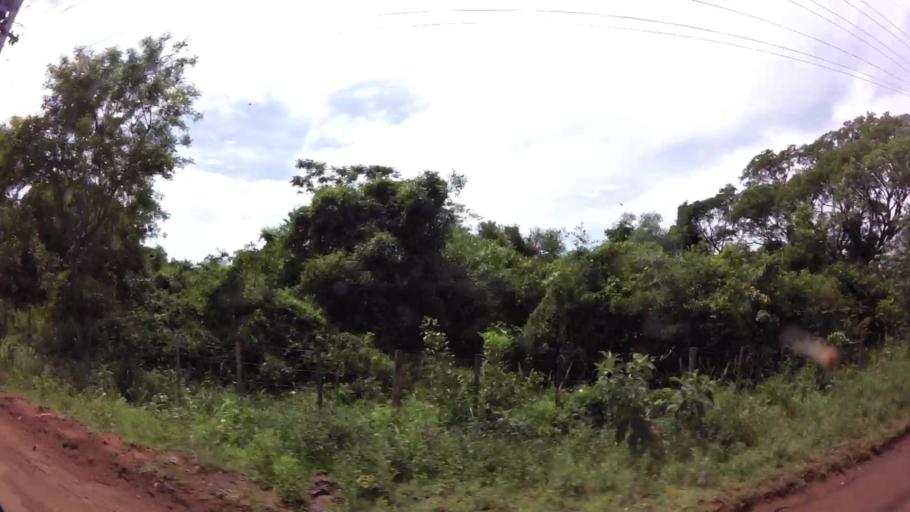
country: PY
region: Central
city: Limpio
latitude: -25.1756
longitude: -57.4418
